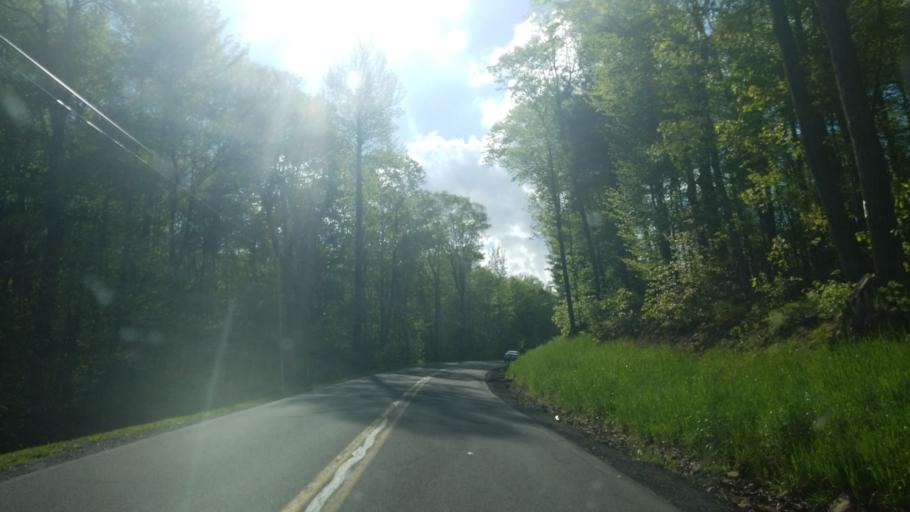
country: US
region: Pennsylvania
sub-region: Clearfield County
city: Osceola Mills
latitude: 40.9342
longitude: -78.3108
